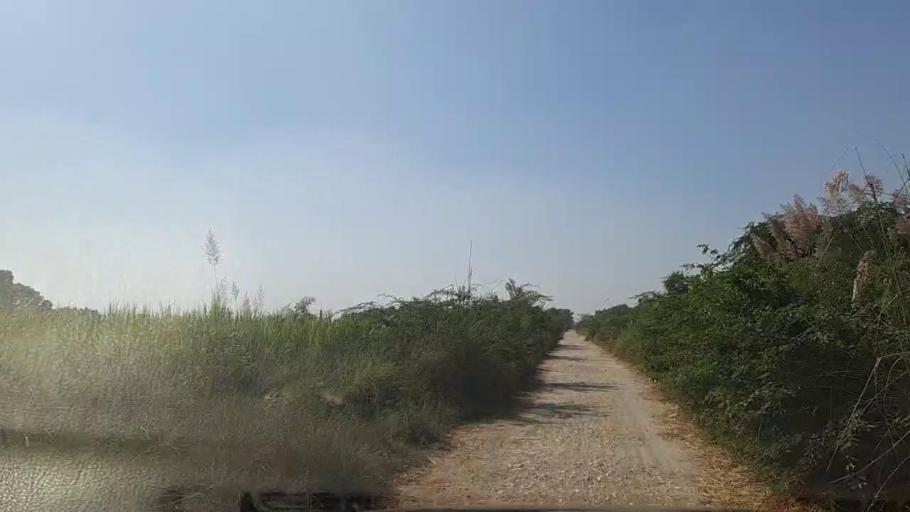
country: PK
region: Sindh
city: Daro Mehar
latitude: 24.8380
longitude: 68.1221
